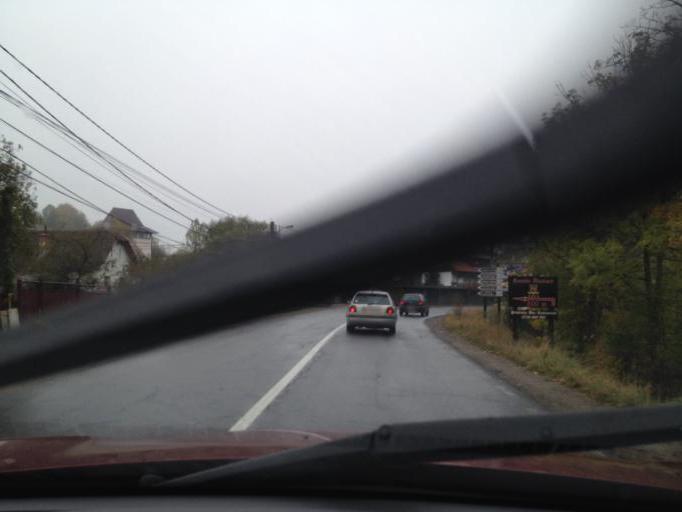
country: RO
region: Brasov
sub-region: Comuna Bran
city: Bran
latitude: 45.5193
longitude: 25.3706
